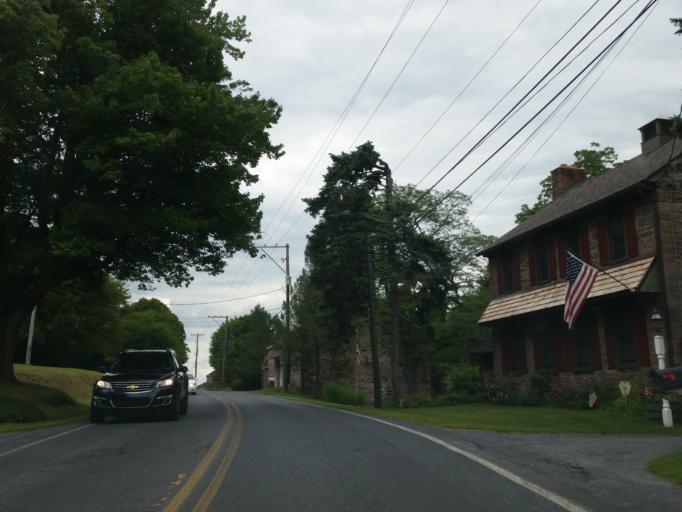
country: US
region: Pennsylvania
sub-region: Lancaster County
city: Adamstown
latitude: 40.2461
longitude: -76.0222
